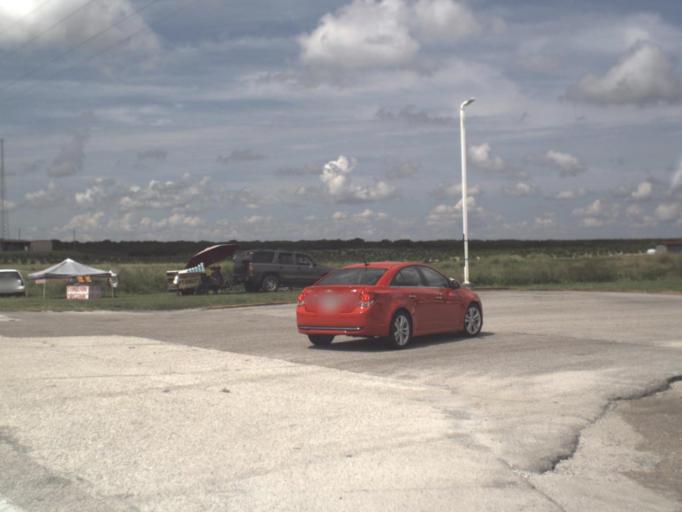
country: US
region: Florida
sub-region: Highlands County
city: Placid Lakes
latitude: 27.2085
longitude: -81.3293
